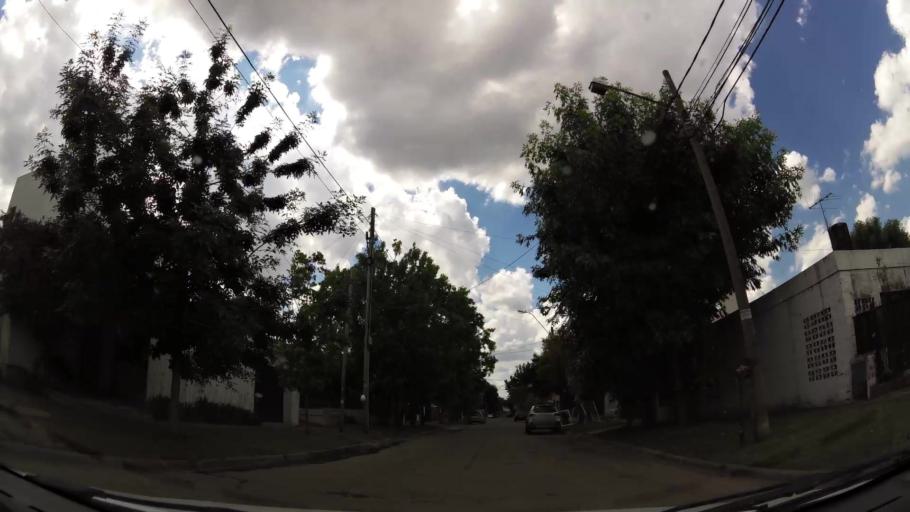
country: AR
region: Buenos Aires
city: Ituzaingo
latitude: -34.6512
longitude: -58.6664
